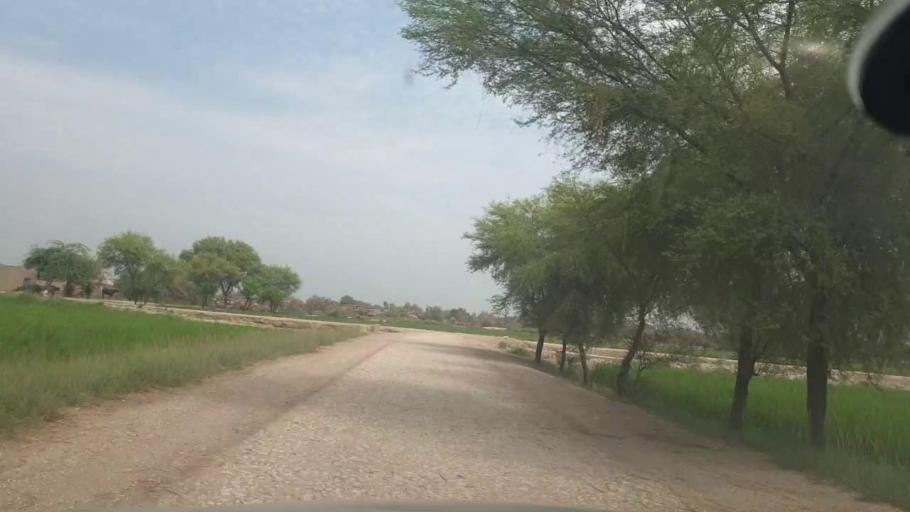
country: PK
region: Sindh
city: Jacobabad
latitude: 28.2510
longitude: 68.5427
